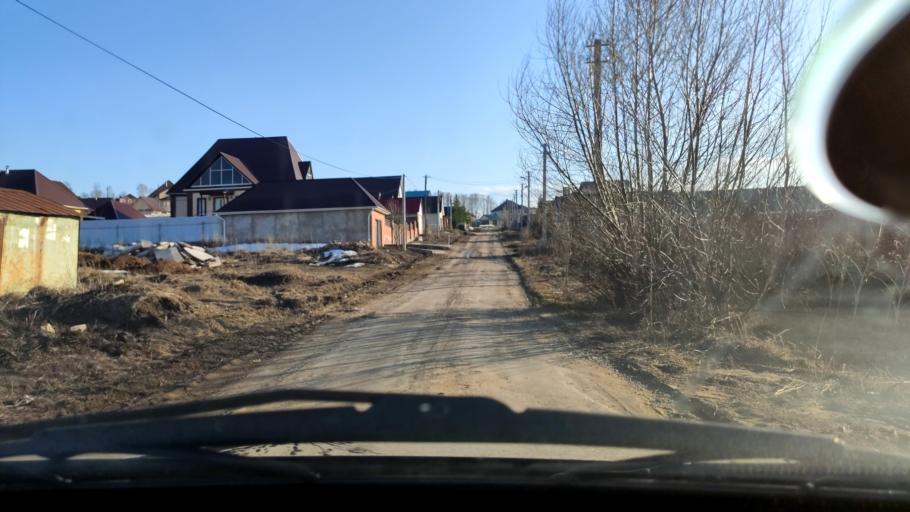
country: RU
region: Bashkortostan
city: Kabakovo
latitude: 54.6338
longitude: 56.0672
